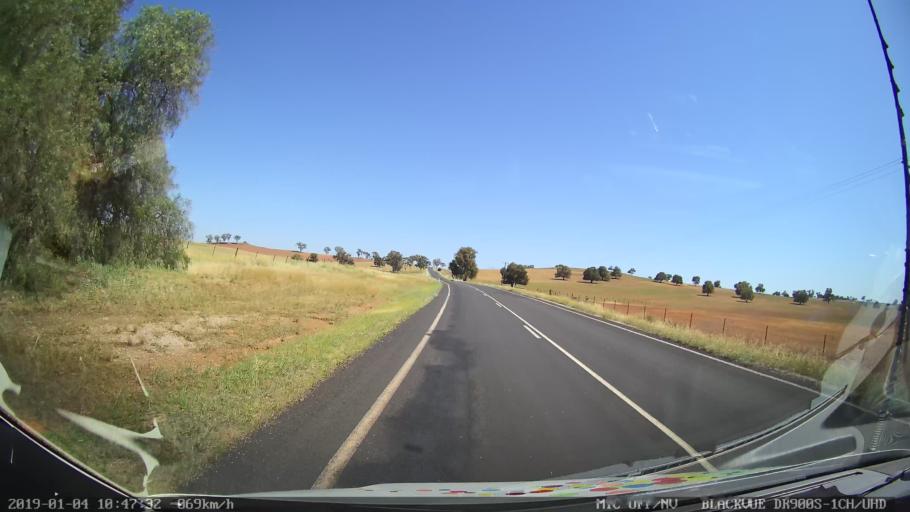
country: AU
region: New South Wales
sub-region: Cabonne
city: Molong
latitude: -33.2691
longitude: 148.7192
